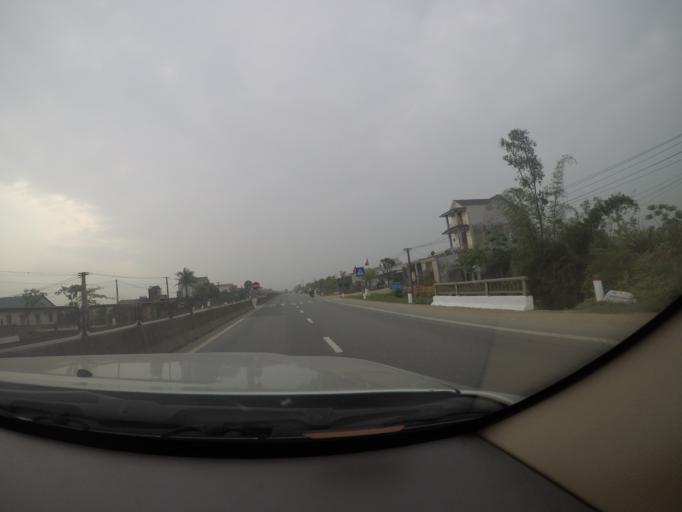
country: VN
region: Ha Tinh
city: Ky Anh
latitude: 18.1750
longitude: 106.2156
